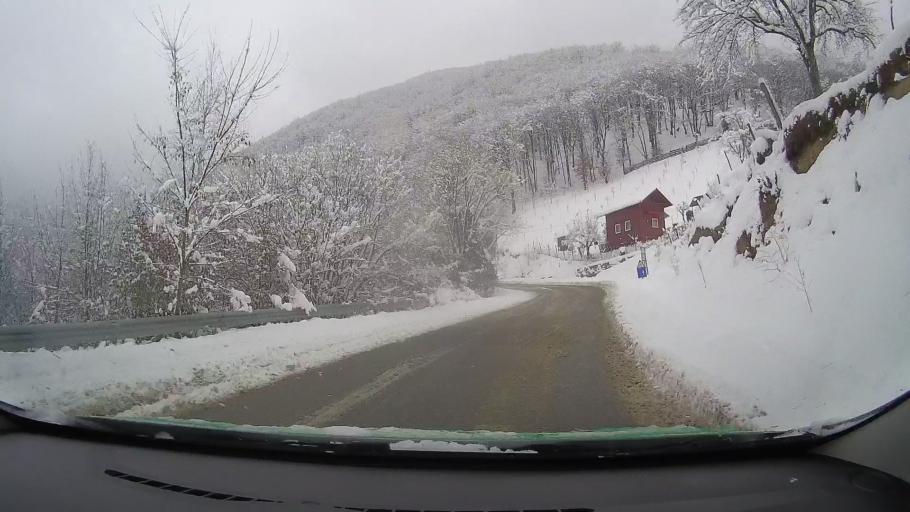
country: RO
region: Alba
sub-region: Comuna Sugag
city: Dobra
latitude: 45.7573
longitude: 23.6636
